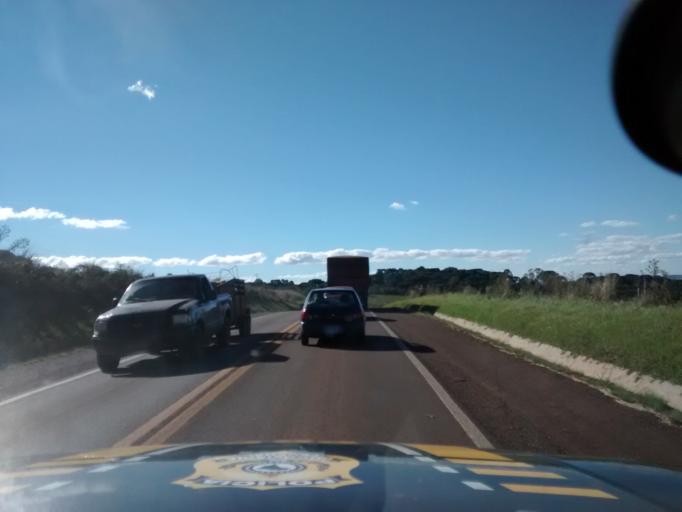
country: BR
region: Rio Grande do Sul
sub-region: Lagoa Vermelha
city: Lagoa Vermelha
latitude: -28.2914
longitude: -51.4632
